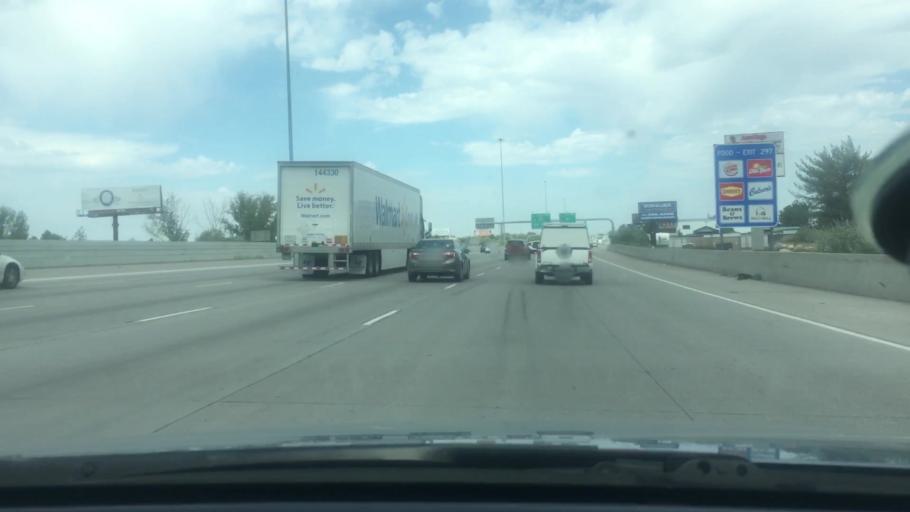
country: US
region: Utah
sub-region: Salt Lake County
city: Midvale
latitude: 40.5937
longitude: -111.9023
